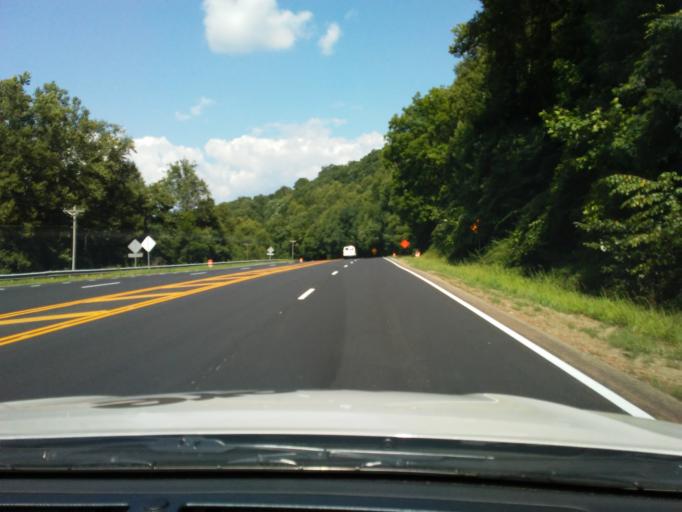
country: US
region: Georgia
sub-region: Towns County
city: Hiawassee
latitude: 34.9668
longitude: -83.8338
